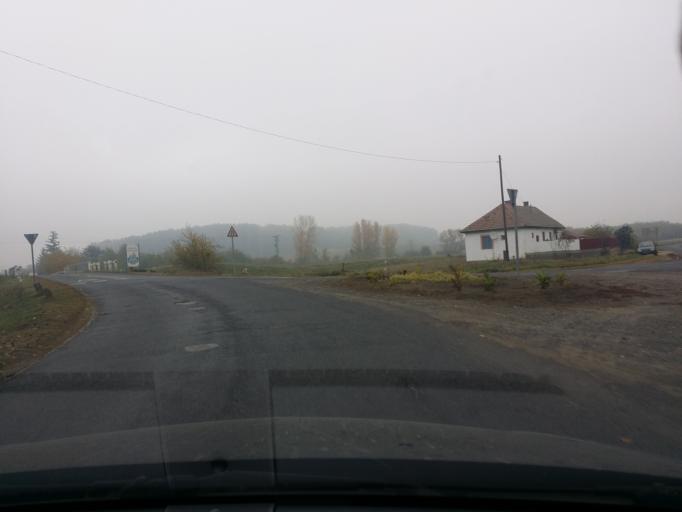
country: HU
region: Szabolcs-Szatmar-Bereg
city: Kek
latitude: 48.0965
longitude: 21.8831
